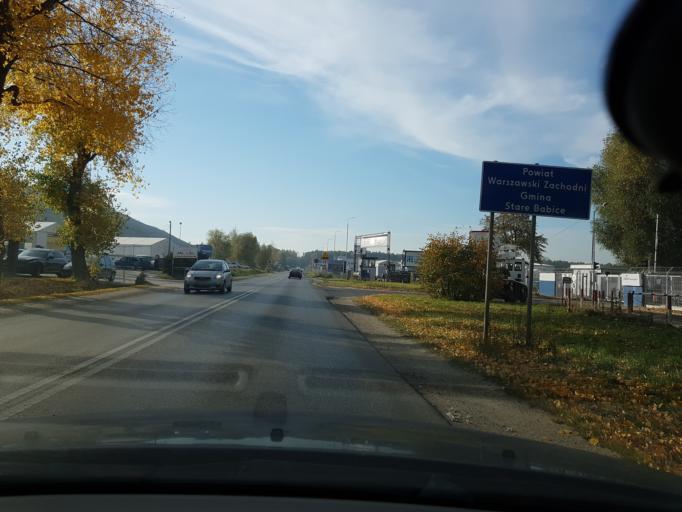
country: PL
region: Masovian Voivodeship
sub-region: Powiat warszawski zachodni
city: Babice
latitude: 52.2804
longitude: 20.8758
